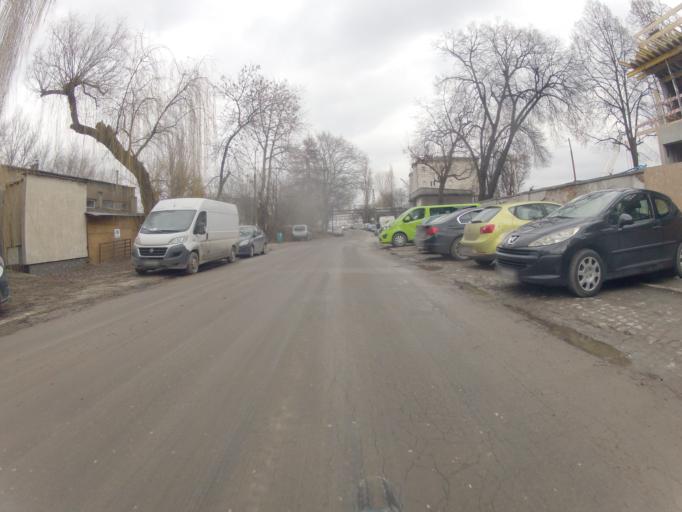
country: PL
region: Lesser Poland Voivodeship
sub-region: Krakow
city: Krakow
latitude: 50.0634
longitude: 19.9728
